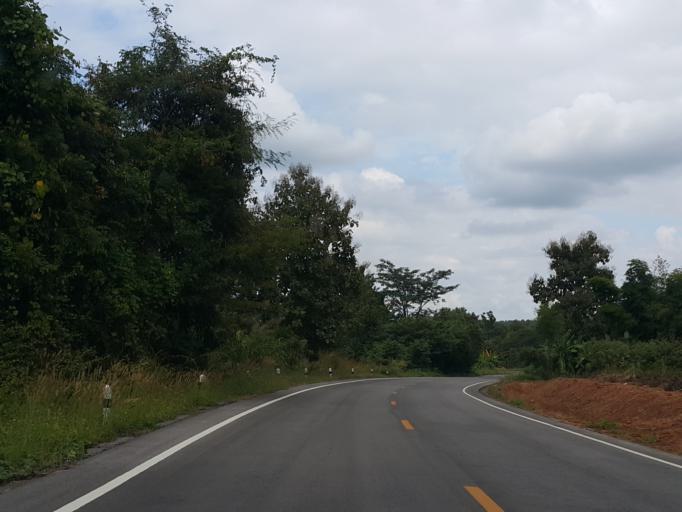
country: TH
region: Lampang
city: Chae Hom
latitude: 18.6208
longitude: 99.4832
